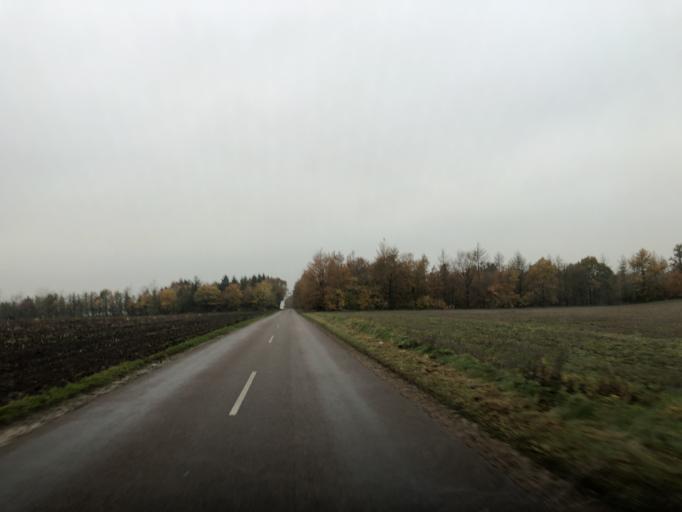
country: DK
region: Central Jutland
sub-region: Herning Kommune
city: Avlum
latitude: 56.2474
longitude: 8.8671
